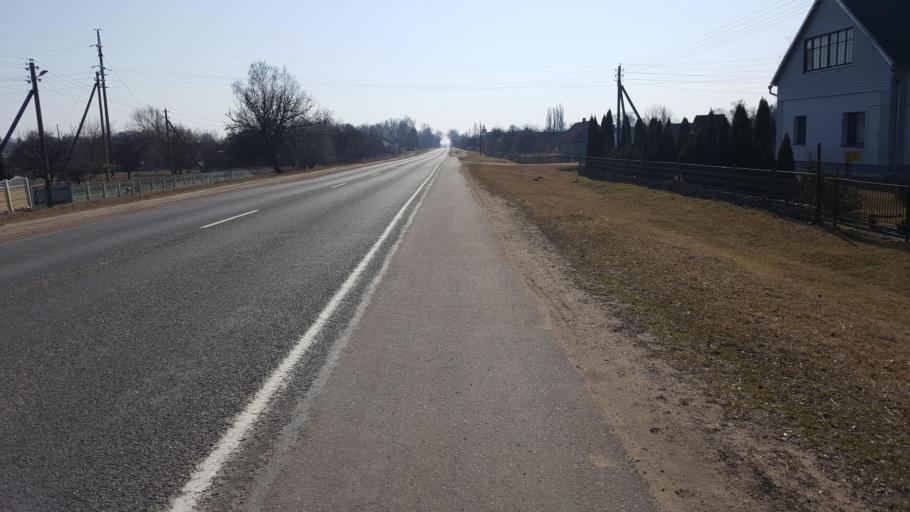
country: BY
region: Brest
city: Kamyanyets
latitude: 52.3211
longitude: 23.9185
